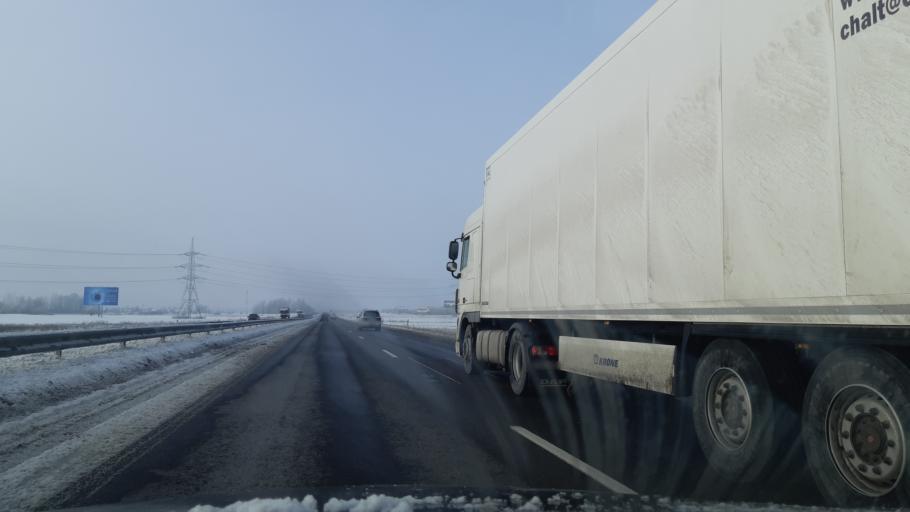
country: LT
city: Kaisiadorys
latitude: 54.8676
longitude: 24.2468
